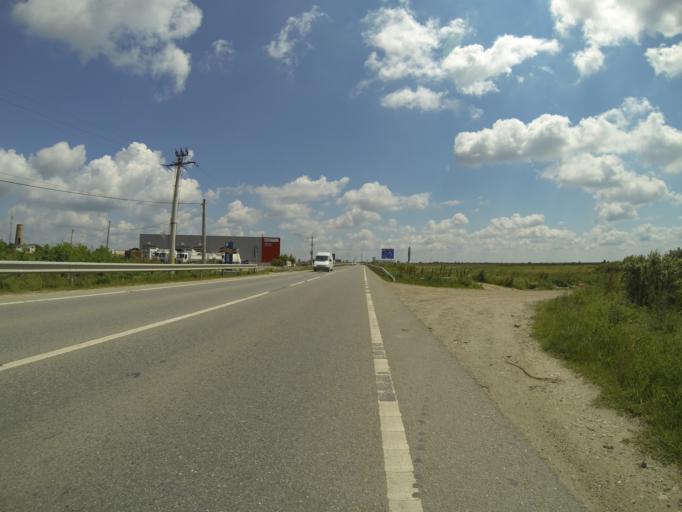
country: RO
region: Dolj
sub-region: Comuna Carcea
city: Carcea
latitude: 44.2628
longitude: 23.9027
